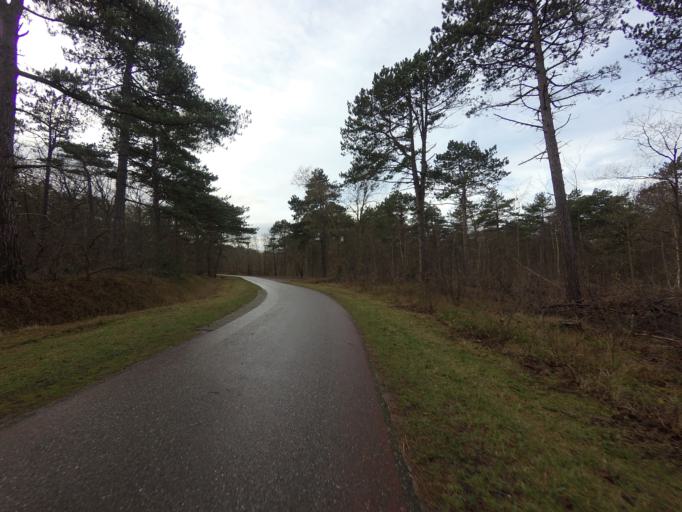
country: NL
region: North Holland
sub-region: Gemeente Texel
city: Den Burg
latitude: 53.0519
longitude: 4.7345
